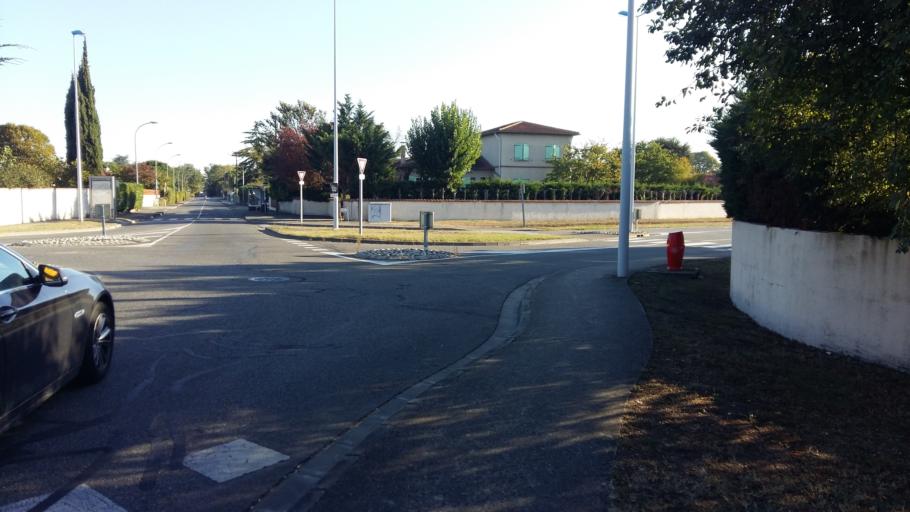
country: FR
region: Midi-Pyrenees
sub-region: Departement de la Haute-Garonne
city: Tournefeuille
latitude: 43.5947
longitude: 1.3256
